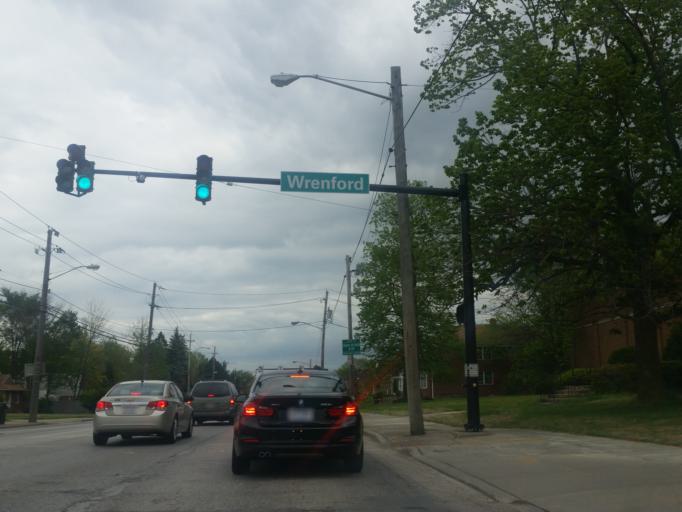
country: US
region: Ohio
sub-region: Cuyahoga County
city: University Heights
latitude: 41.5013
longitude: -81.5267
